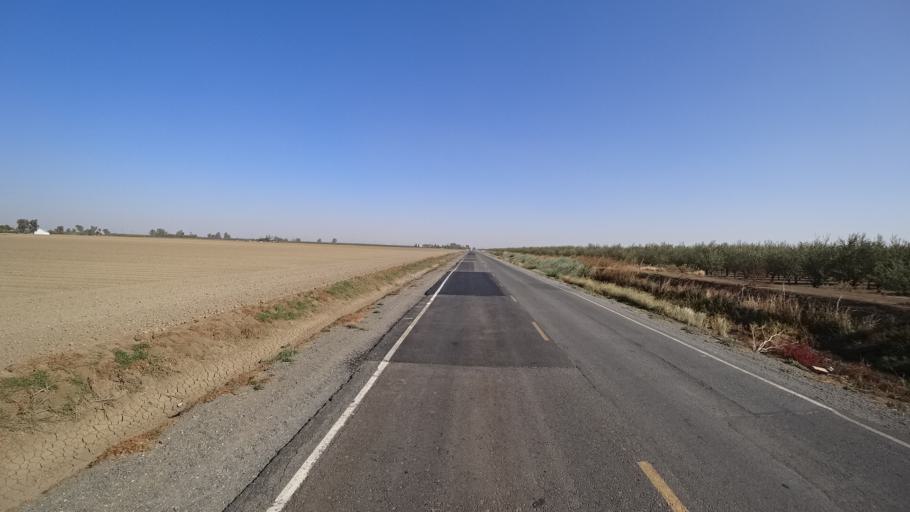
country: US
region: California
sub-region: Yolo County
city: Esparto
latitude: 38.7326
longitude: -122.0005
